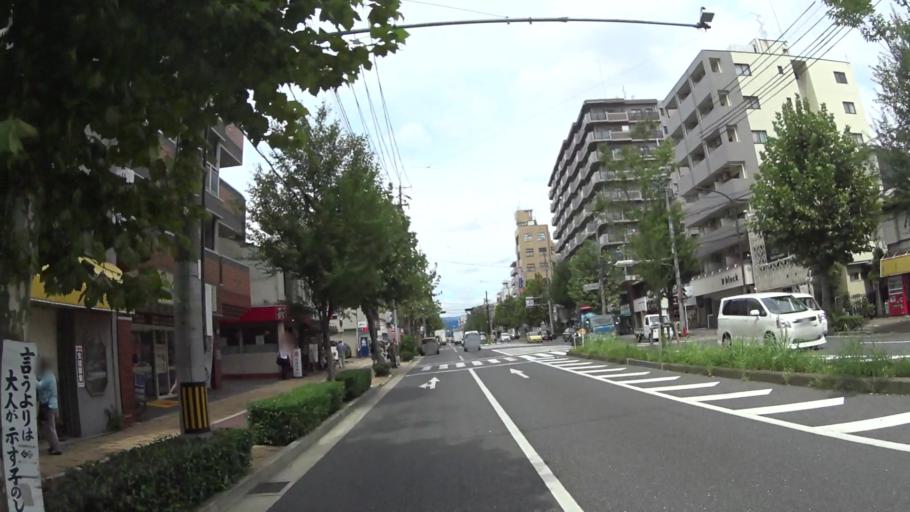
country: JP
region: Kyoto
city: Kyoto
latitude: 35.0056
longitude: 135.7319
